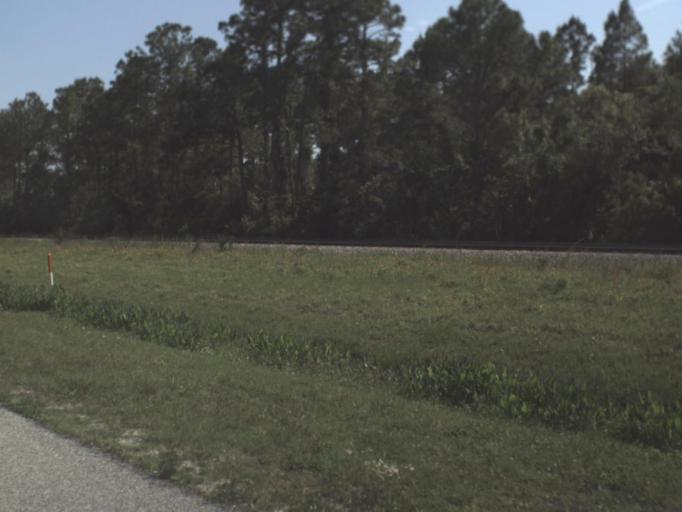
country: US
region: Florida
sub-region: Saint Johns County
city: Villano Beach
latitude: 29.9517
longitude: -81.3421
